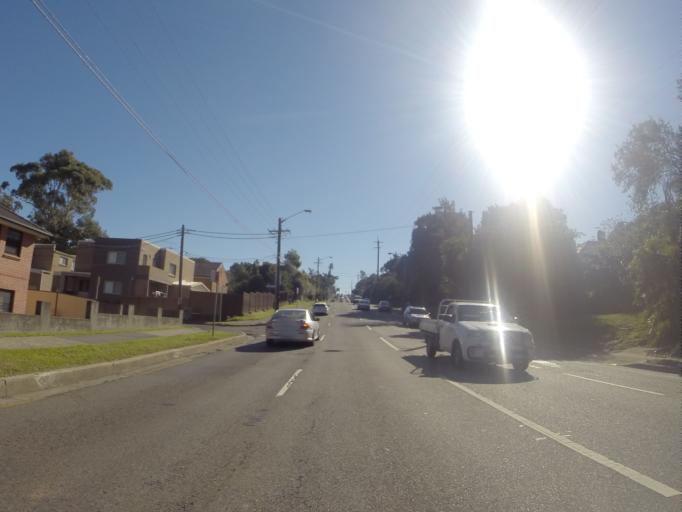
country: AU
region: New South Wales
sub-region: Kogarah
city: Hurstville Grove
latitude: -33.9686
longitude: 151.0970
